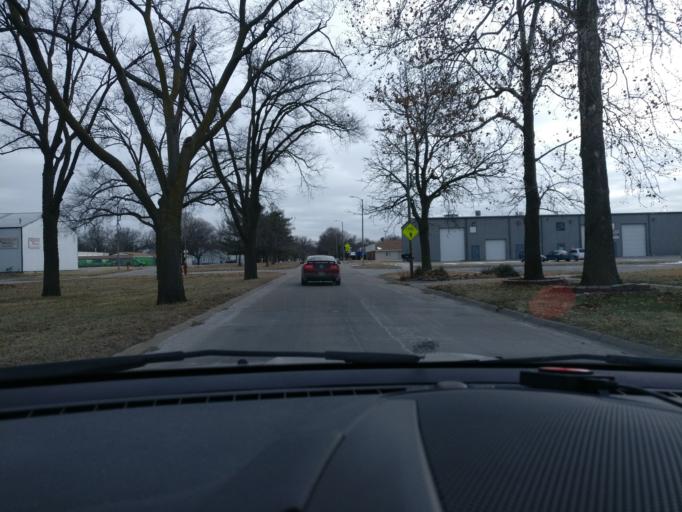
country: US
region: Nebraska
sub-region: Lancaster County
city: Lincoln
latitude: 40.8522
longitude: -96.6402
